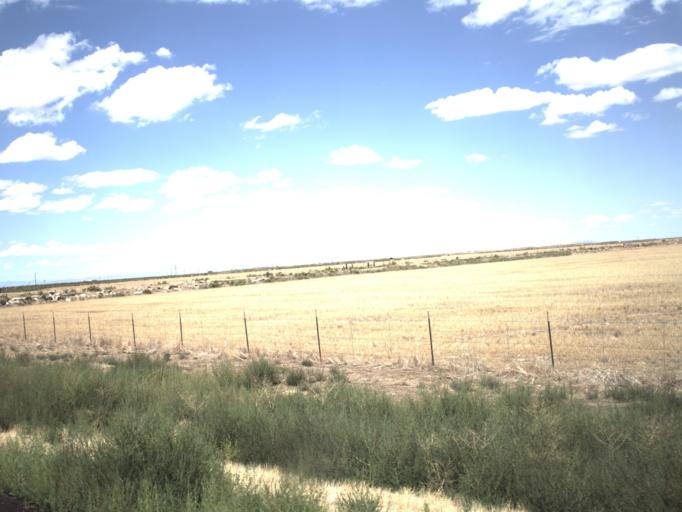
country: US
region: Utah
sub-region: Millard County
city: Fillmore
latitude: 39.1181
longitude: -112.3492
